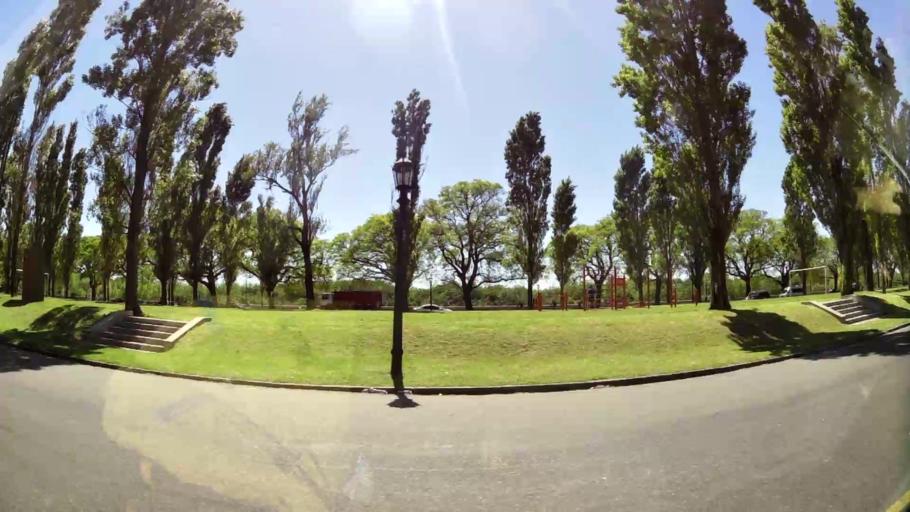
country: AR
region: Buenos Aires F.D.
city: Buenos Aires
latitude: -34.6017
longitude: -58.3626
